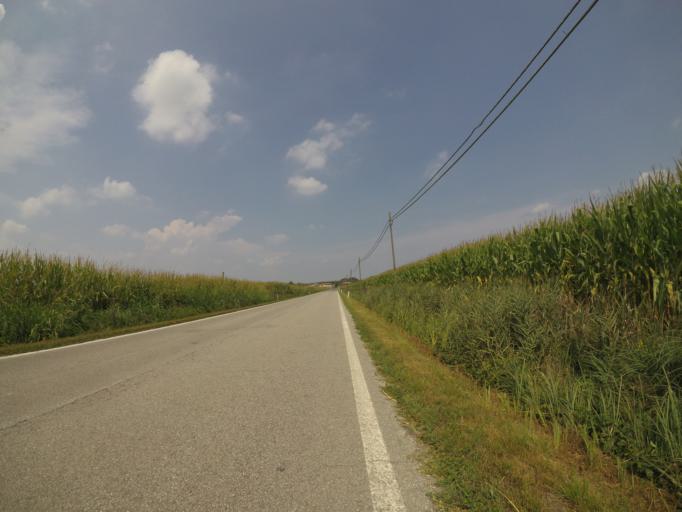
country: IT
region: Friuli Venezia Giulia
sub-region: Provincia di Udine
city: Pocenia
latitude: 45.8406
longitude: 13.0772
